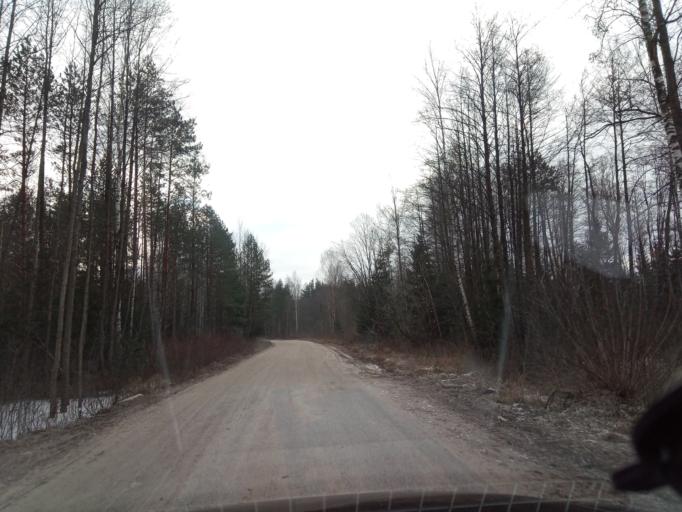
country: LT
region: Alytaus apskritis
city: Varena
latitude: 54.0225
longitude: 24.3463
